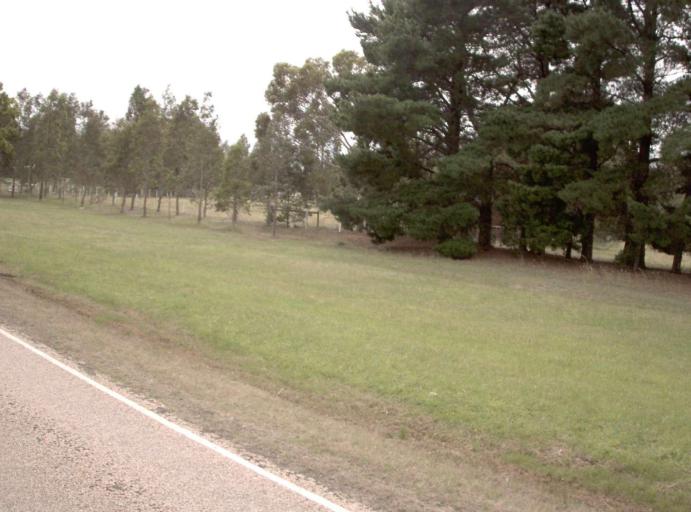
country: AU
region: Victoria
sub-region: Wellington
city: Sale
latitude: -37.9528
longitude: 147.0865
